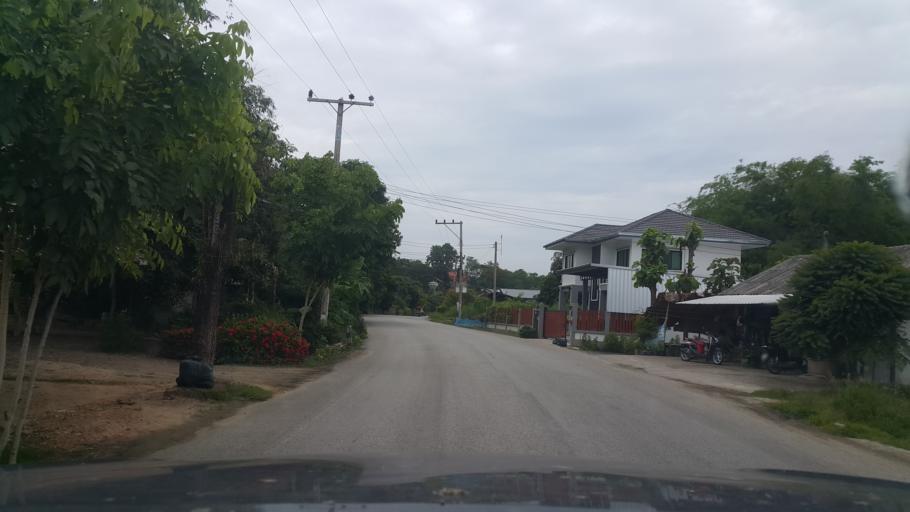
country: TH
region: Chiang Mai
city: San Pa Tong
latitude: 18.6589
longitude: 98.8355
